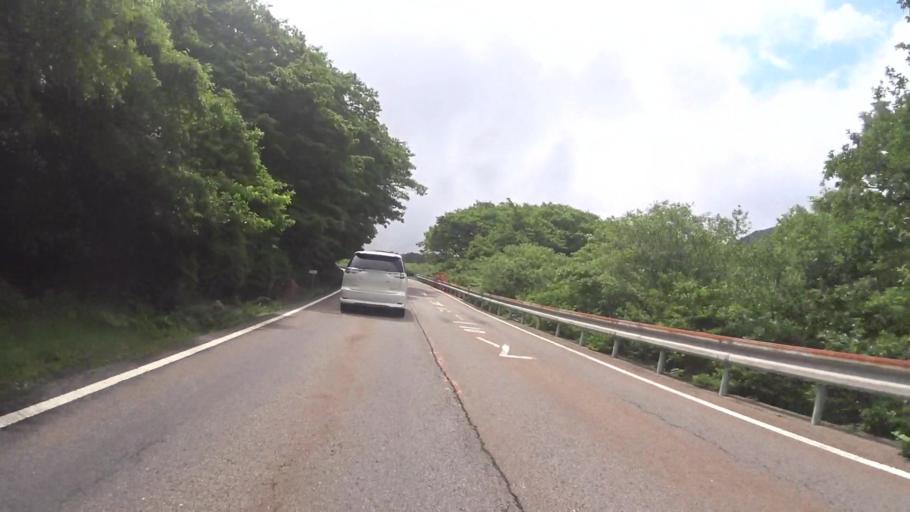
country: JP
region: Oita
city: Tsukawaki
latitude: 33.0981
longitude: 131.2130
